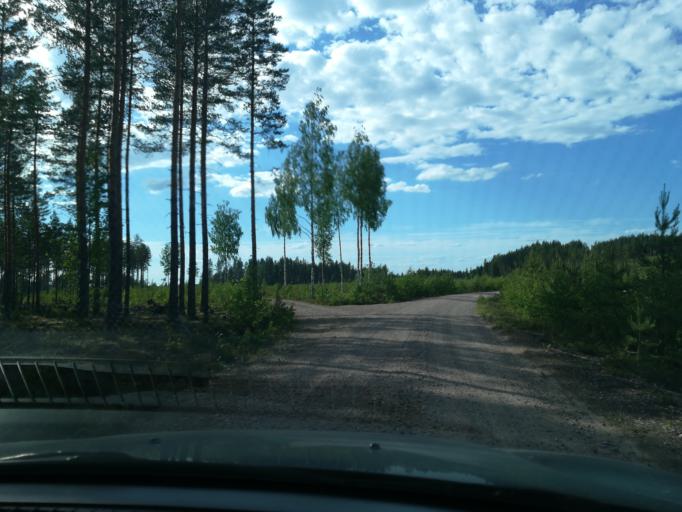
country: FI
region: Southern Savonia
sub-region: Savonlinna
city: Savonlinna
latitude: 61.6369
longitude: 28.7280
